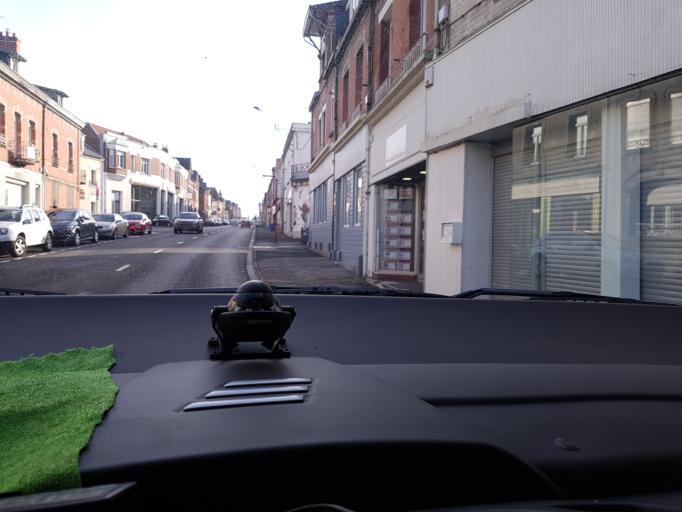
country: FR
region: Picardie
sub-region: Departement de l'Aisne
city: Hirson
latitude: 49.9224
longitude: 4.0828
